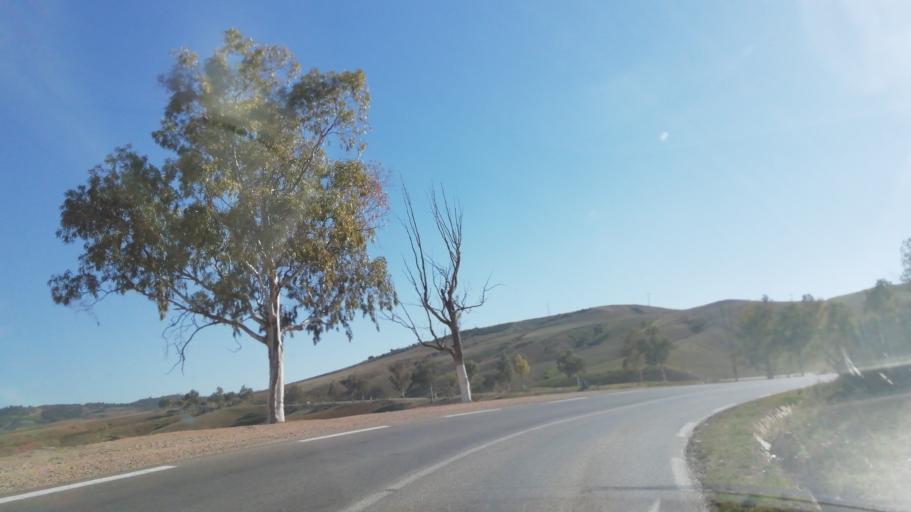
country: DZ
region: Tlemcen
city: Nedroma
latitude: 34.8298
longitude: -1.6471
